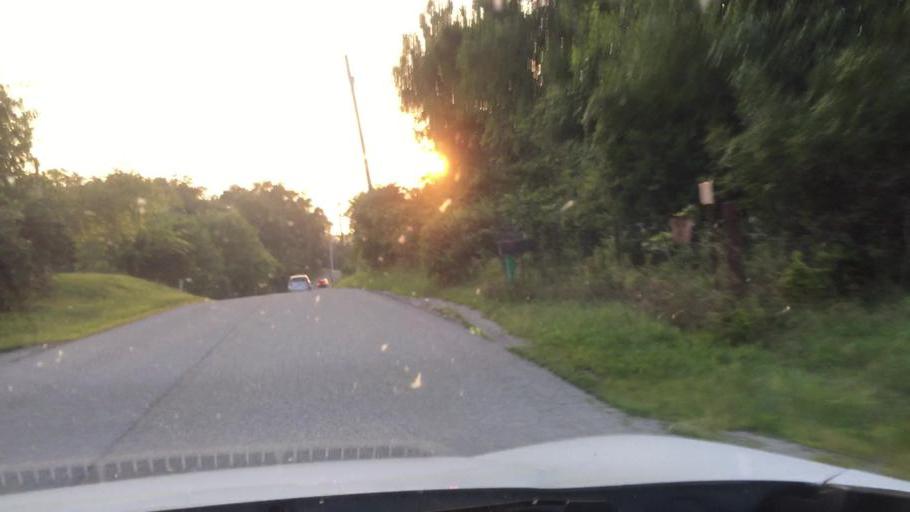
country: US
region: Ohio
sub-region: Clark County
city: Lisbon
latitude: 39.9445
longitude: -83.5924
